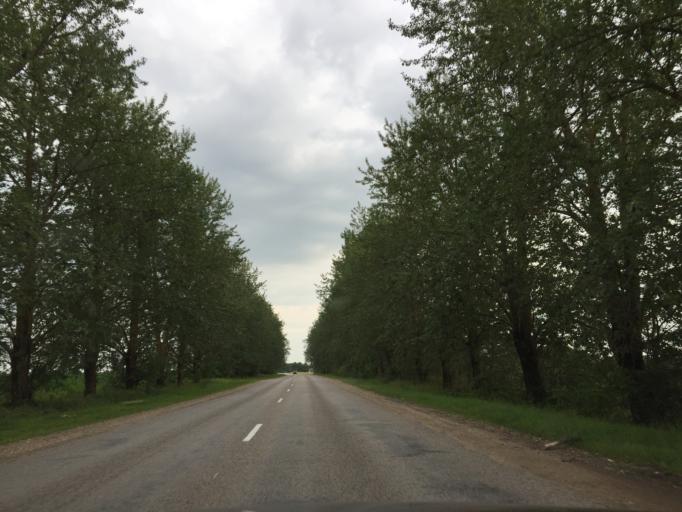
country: LV
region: Dobeles Rajons
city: Dobele
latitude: 56.5780
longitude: 23.2967
